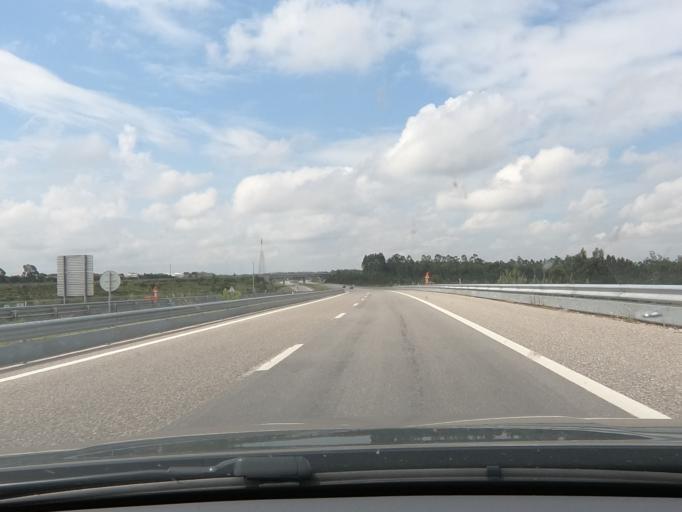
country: PT
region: Leiria
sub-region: Marinha Grande
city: Marinha Grande
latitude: 39.7438
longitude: -8.8833
